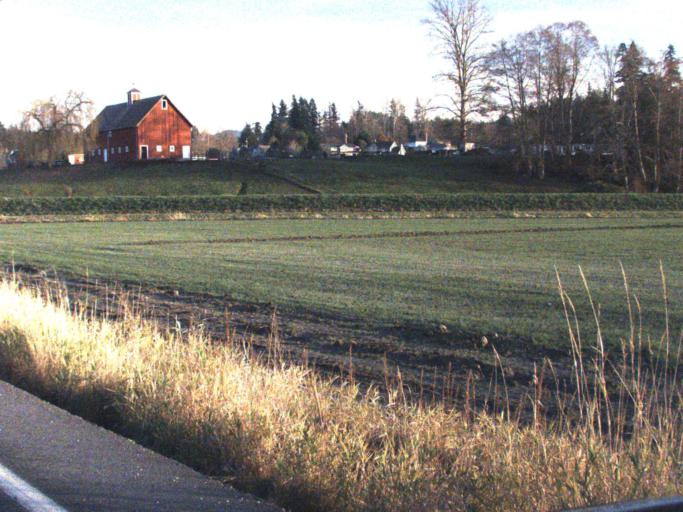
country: US
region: Washington
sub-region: Skagit County
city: Mount Vernon
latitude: 48.3411
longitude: -122.3265
